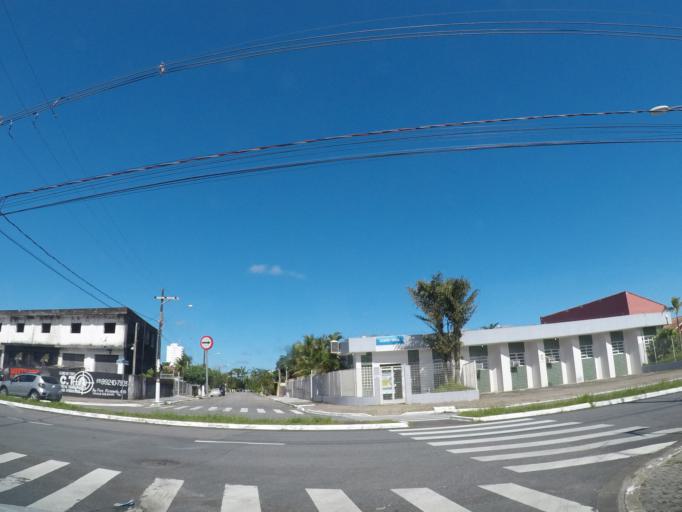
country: BR
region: Sao Paulo
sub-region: Mongagua
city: Mongagua
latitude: -24.0662
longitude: -46.5683
